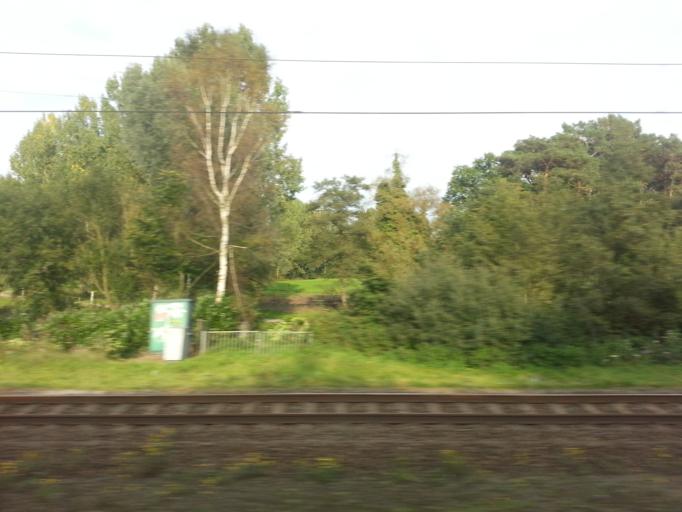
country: NL
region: North Brabant
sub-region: Gemeente Boxtel
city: Boxtel
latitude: 51.5555
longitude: 5.3474
